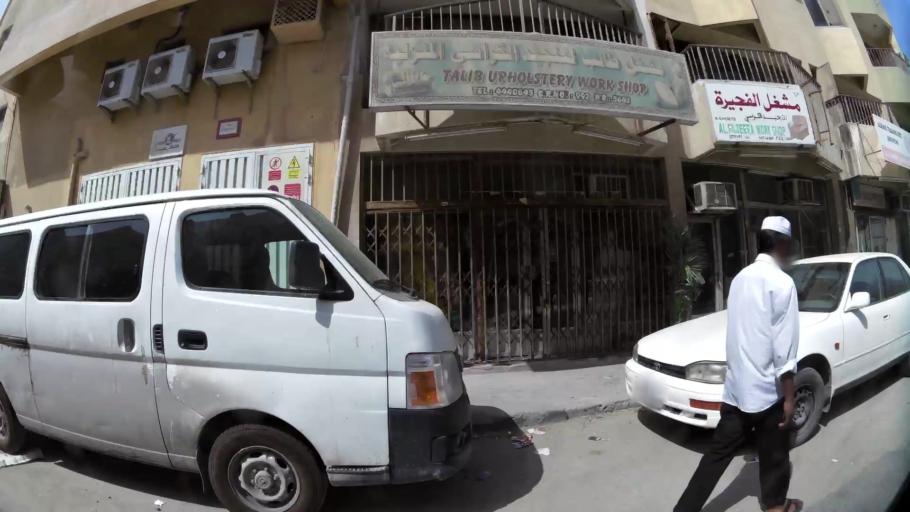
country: QA
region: Baladiyat ad Dawhah
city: Doha
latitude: 25.2804
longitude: 51.5322
